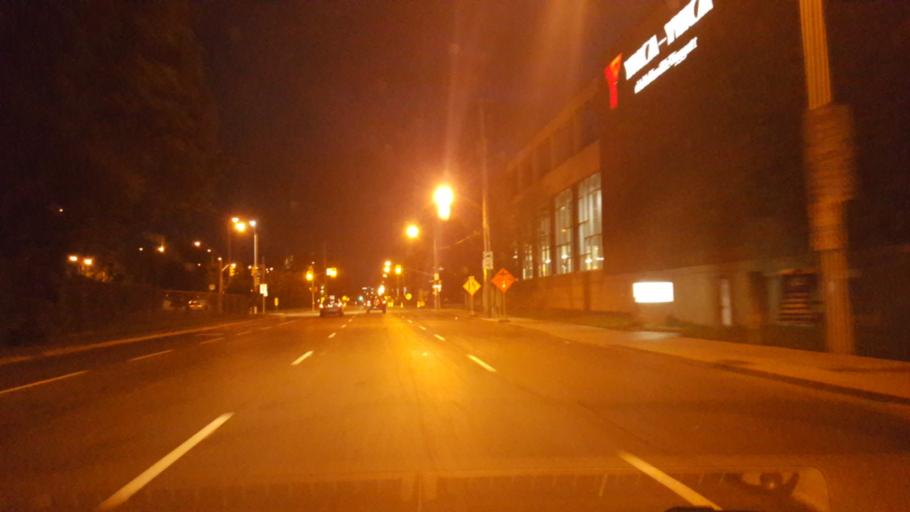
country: CA
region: Ontario
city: Ottawa
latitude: 45.4111
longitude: -75.6884
